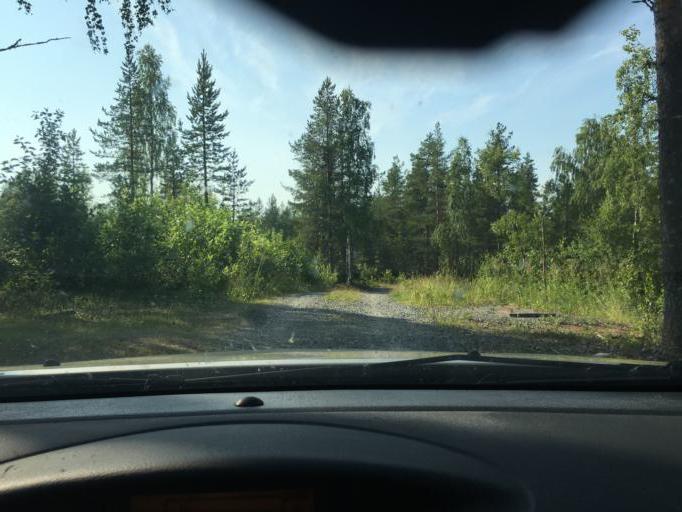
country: SE
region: Norrbotten
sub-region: Kalix Kommun
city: Toere
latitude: 65.8688
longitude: 22.6424
